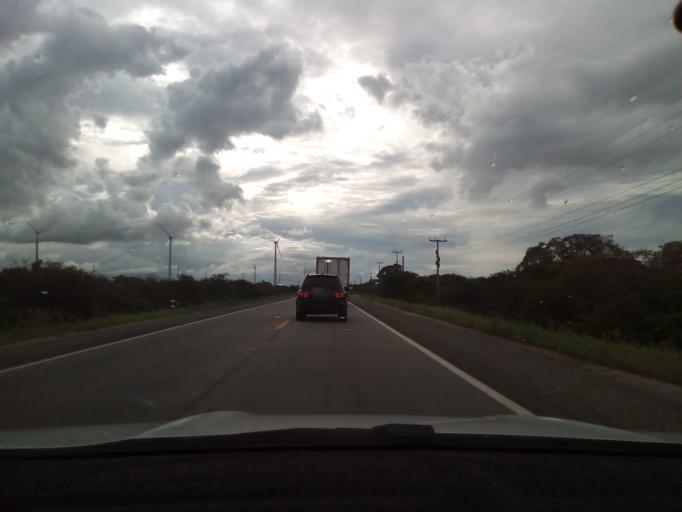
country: BR
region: Ceara
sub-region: Aracati
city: Aracati
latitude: -4.5975
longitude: -37.6756
